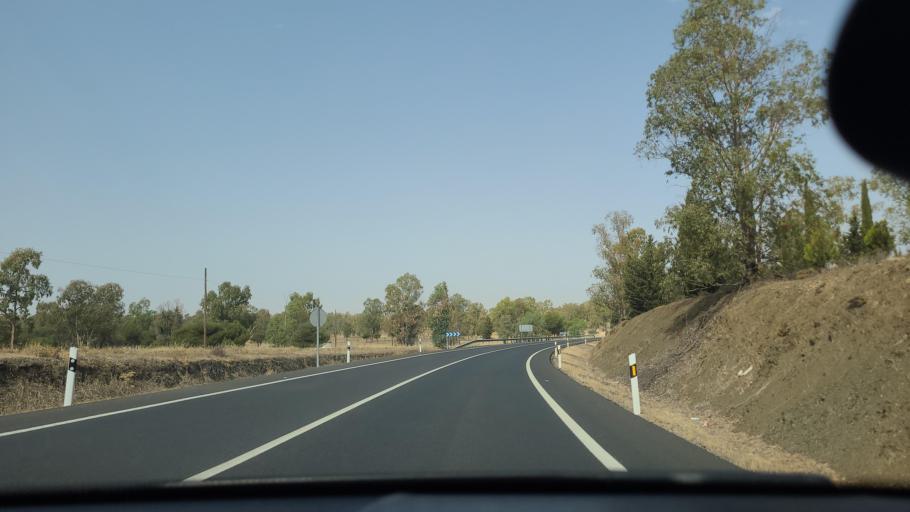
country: ES
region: Extremadura
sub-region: Provincia de Badajoz
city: Berlanga
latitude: 38.2723
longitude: -5.8114
